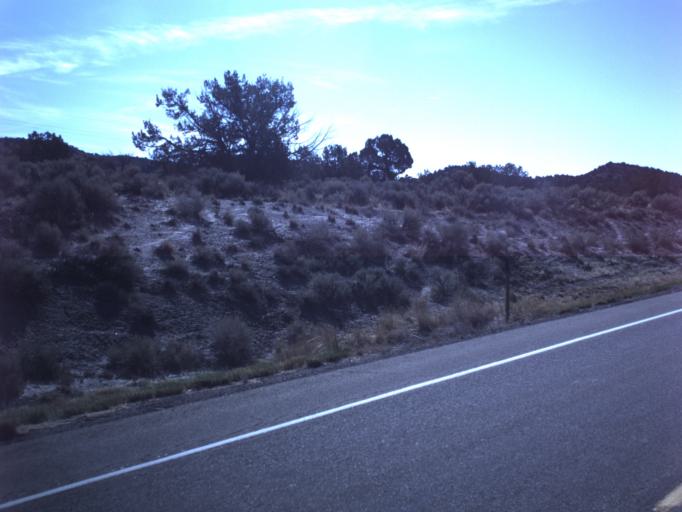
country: US
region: Utah
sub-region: Sanpete County
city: Gunnison
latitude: 39.3676
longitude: -111.9295
